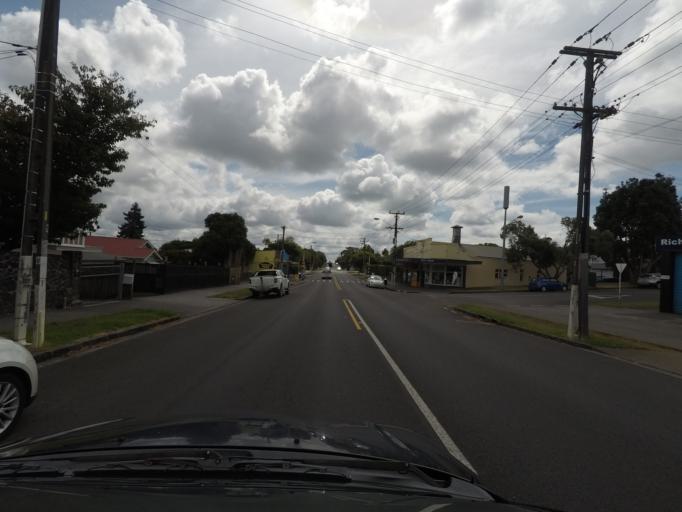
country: NZ
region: Auckland
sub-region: Auckland
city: Rosebank
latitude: -36.8926
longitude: 174.7137
